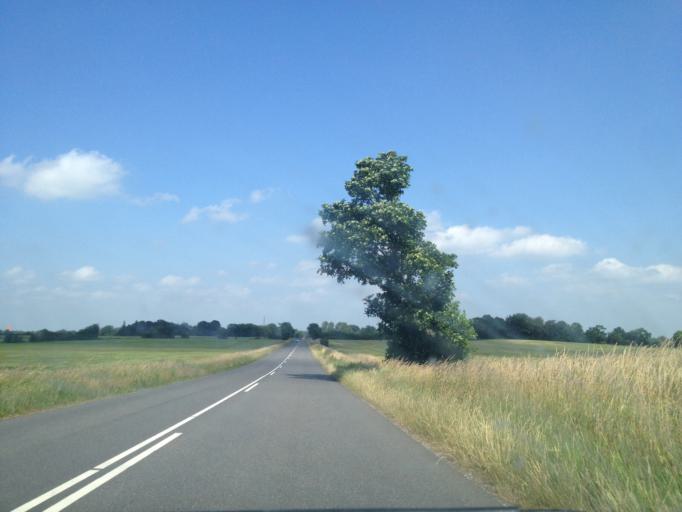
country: DK
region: South Denmark
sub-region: Kolding Kommune
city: Vamdrup
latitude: 55.4122
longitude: 9.2589
